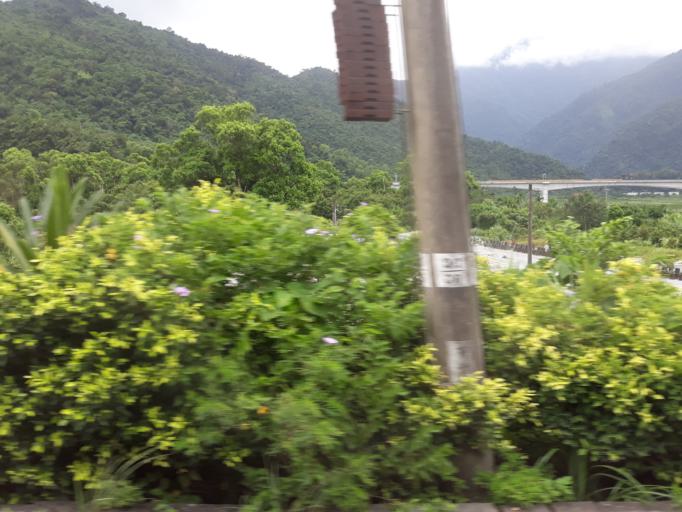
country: TW
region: Taiwan
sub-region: Yilan
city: Yilan
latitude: 24.4383
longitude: 121.7809
